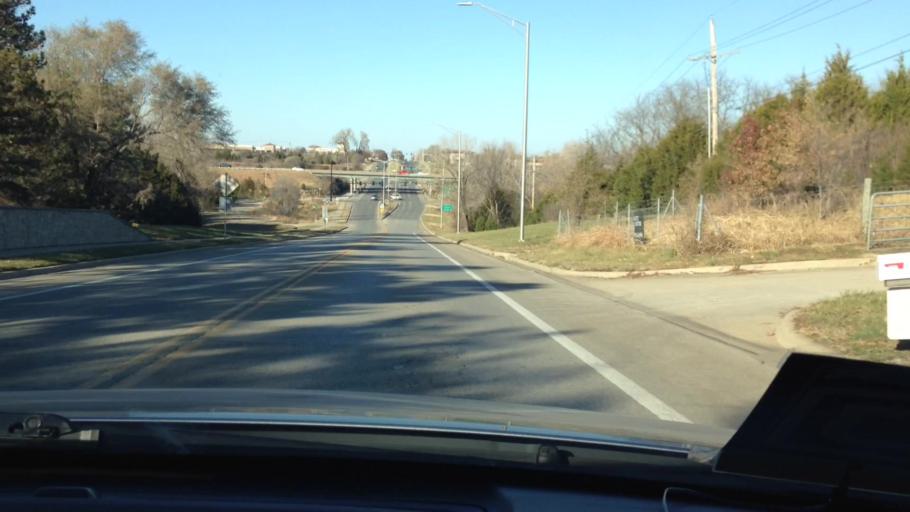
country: US
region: Kansas
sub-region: Johnson County
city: Olathe
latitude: 38.9384
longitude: -94.8161
